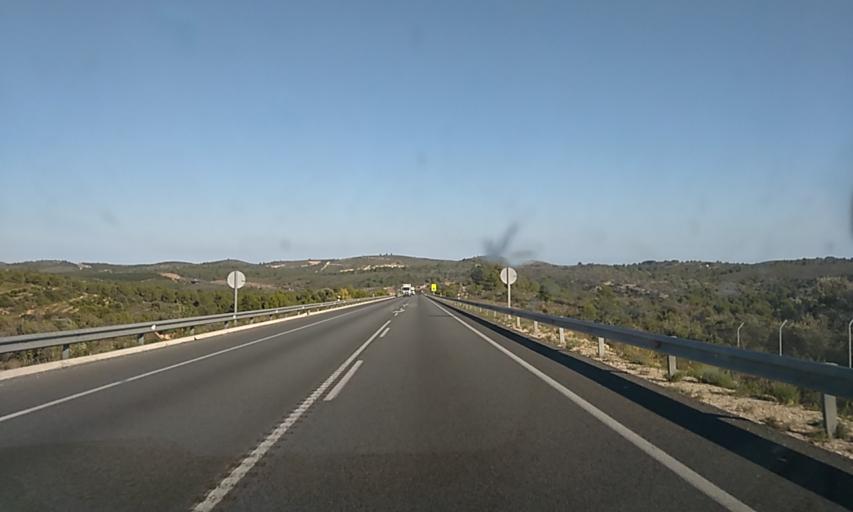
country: ES
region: Valencia
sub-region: Provincia de Castello
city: Torreblanca
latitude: 40.2112
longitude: 0.1273
